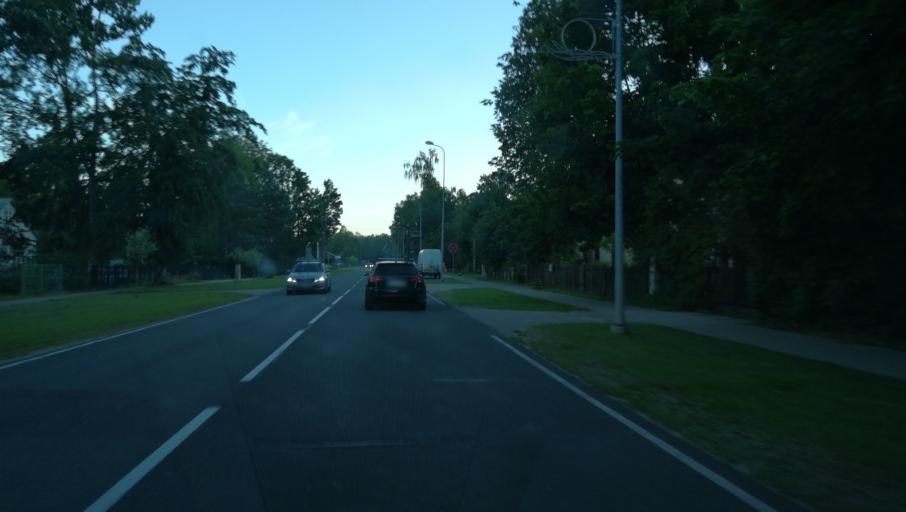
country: LV
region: Saulkrastu
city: Saulkrasti
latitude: 57.2409
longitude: 24.3980
